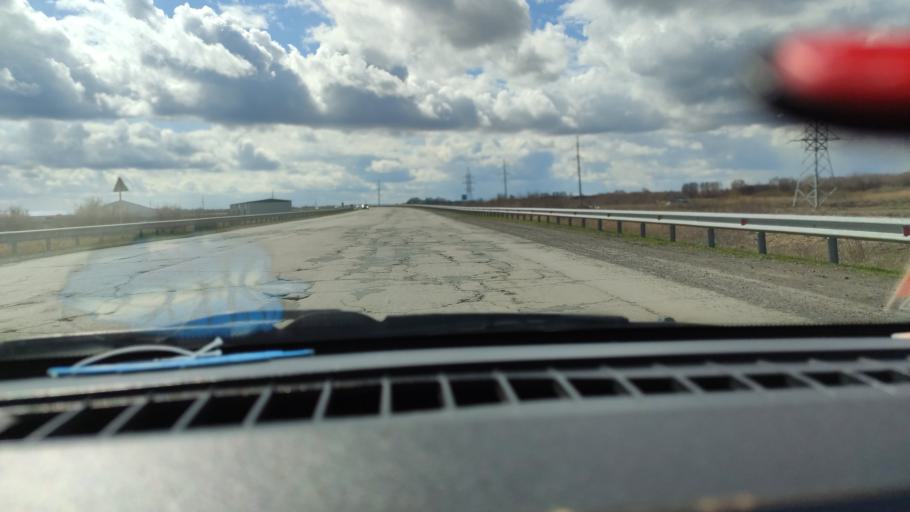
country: RU
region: Samara
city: Tol'yatti
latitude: 53.6702
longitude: 49.4147
